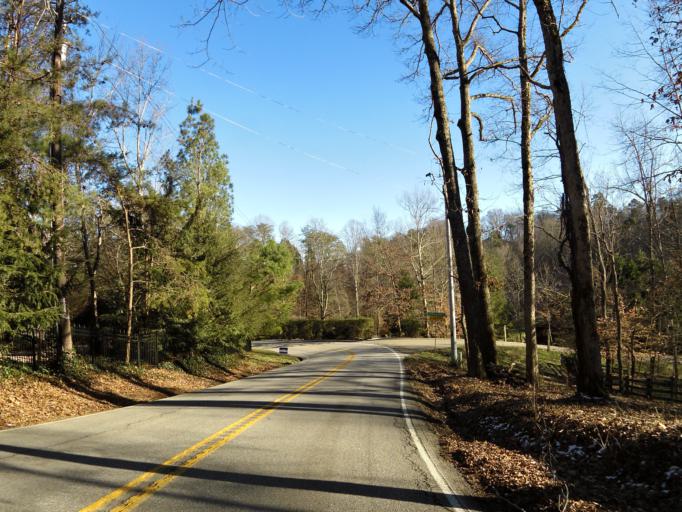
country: US
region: Tennessee
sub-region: Blount County
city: Louisville
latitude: 35.8910
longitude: -83.9945
